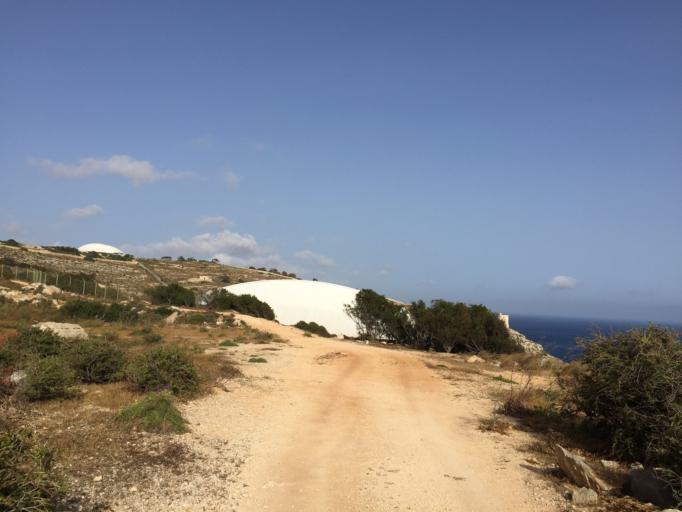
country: MT
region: Il-Qrendi
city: Qrendi
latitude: 35.8270
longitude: 14.4348
